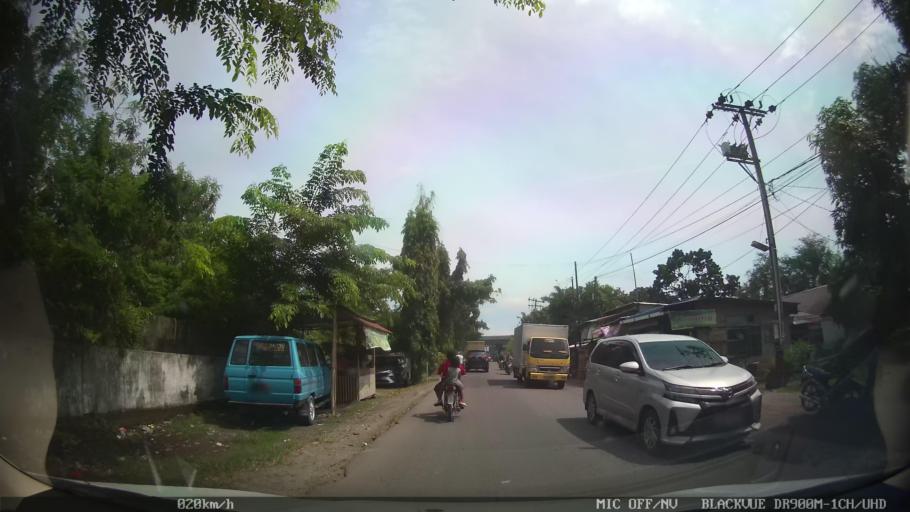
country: ID
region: North Sumatra
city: Medan
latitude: 3.6305
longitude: 98.7160
